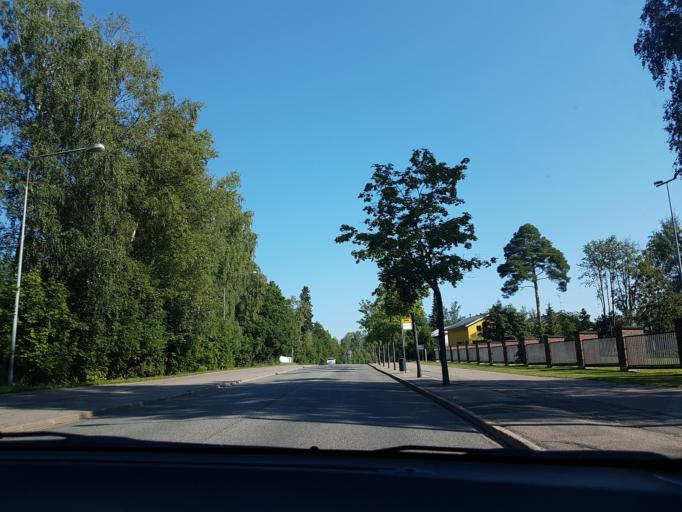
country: FI
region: Uusimaa
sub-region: Helsinki
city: Vantaa
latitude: 60.2641
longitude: 25.0577
